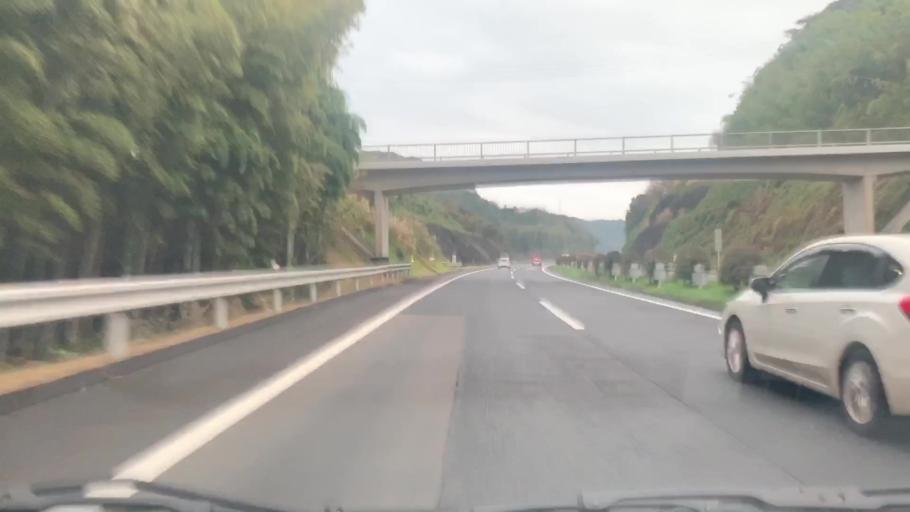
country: JP
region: Nagasaki
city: Omura
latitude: 32.8859
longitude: 129.9943
